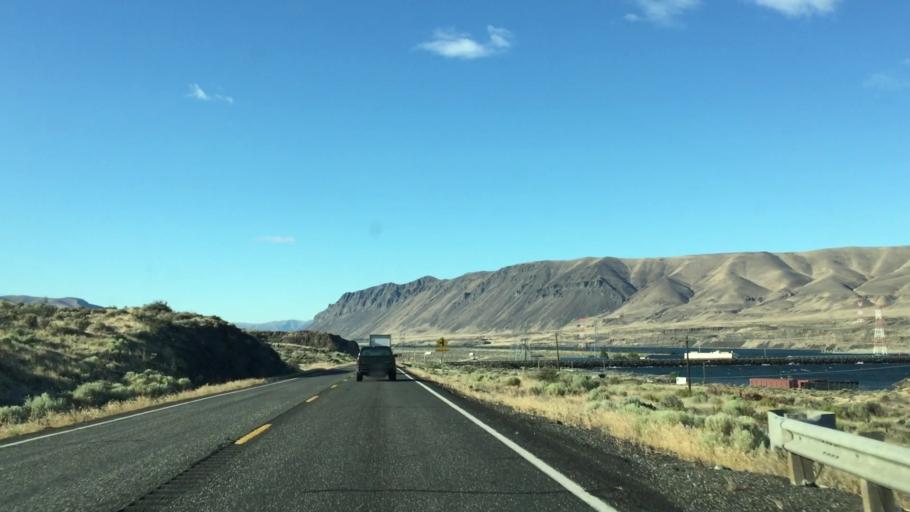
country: US
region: Washington
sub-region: Grant County
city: Mattawa
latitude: 46.8840
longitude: -119.9552
